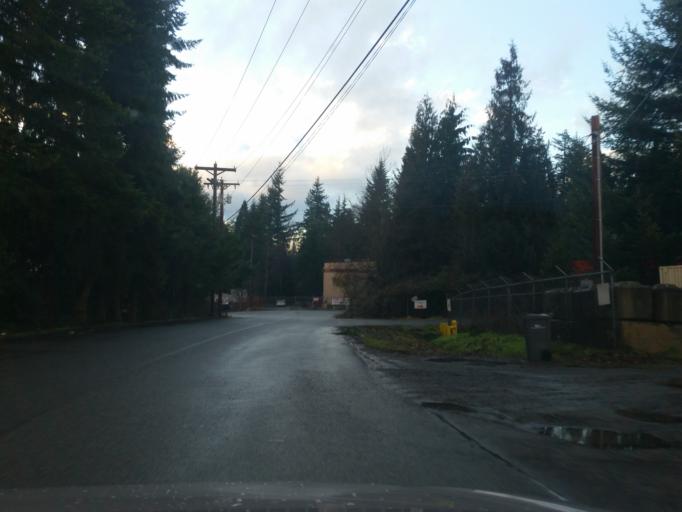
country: US
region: Washington
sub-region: Snohomish County
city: Maltby
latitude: 47.7982
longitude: -122.1198
